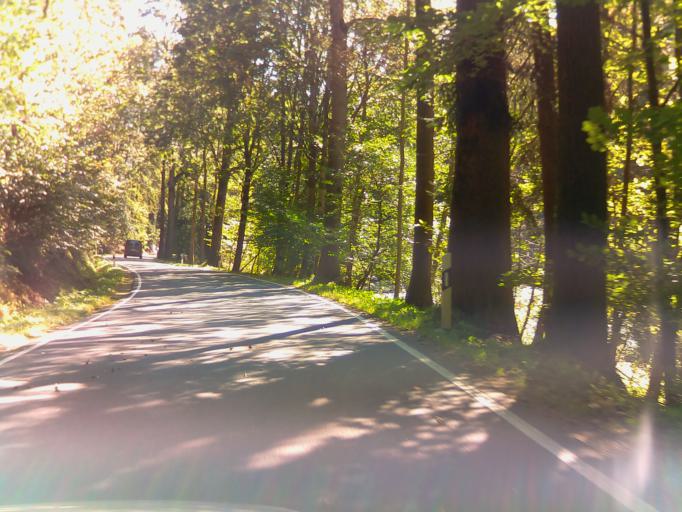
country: DE
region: Thuringia
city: Wurzbach
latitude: 50.4998
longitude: 11.4911
